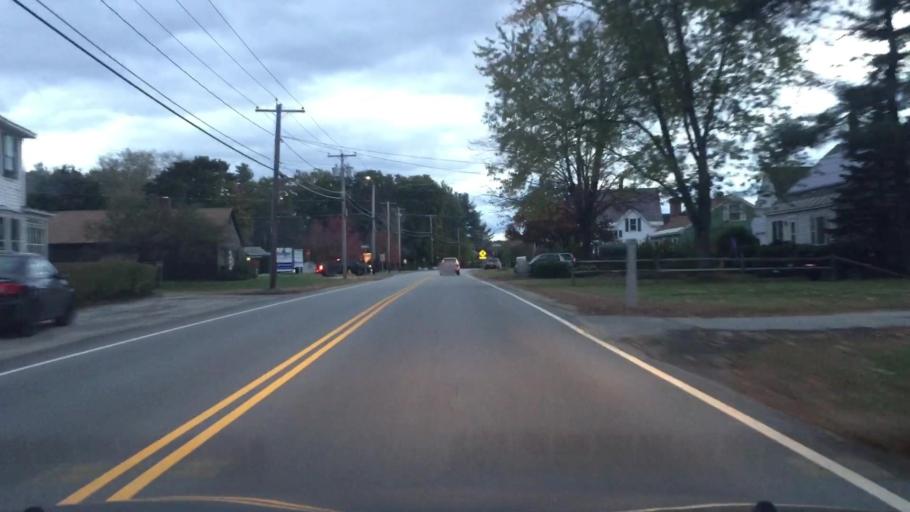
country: US
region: New Hampshire
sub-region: Cheshire County
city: Keene
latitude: 42.9067
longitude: -72.2649
